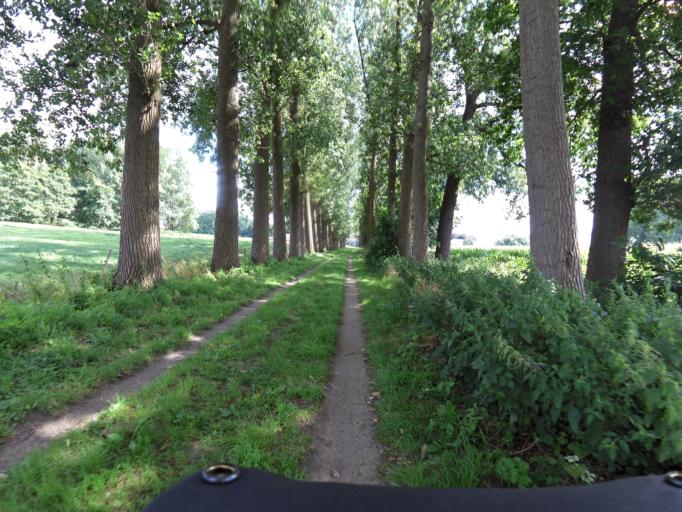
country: BE
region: Flanders
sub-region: Provincie Antwerpen
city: Hoogstraten
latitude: 51.4059
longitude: 4.7775
